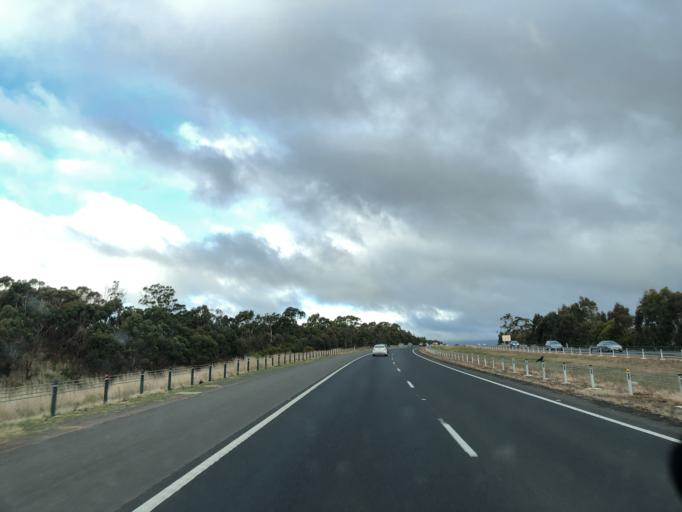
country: AU
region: Victoria
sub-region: Mount Alexander
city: Castlemaine
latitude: -37.2731
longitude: 144.4819
